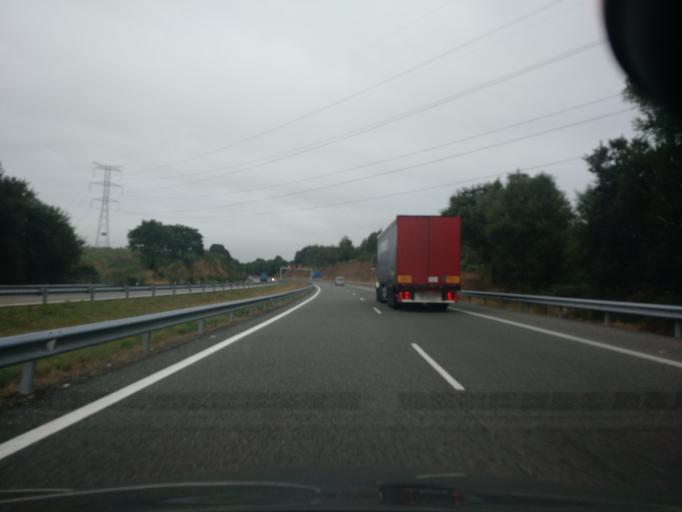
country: ES
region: Galicia
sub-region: Provincia da Coruna
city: Ordes
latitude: 43.1077
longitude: -8.3436
